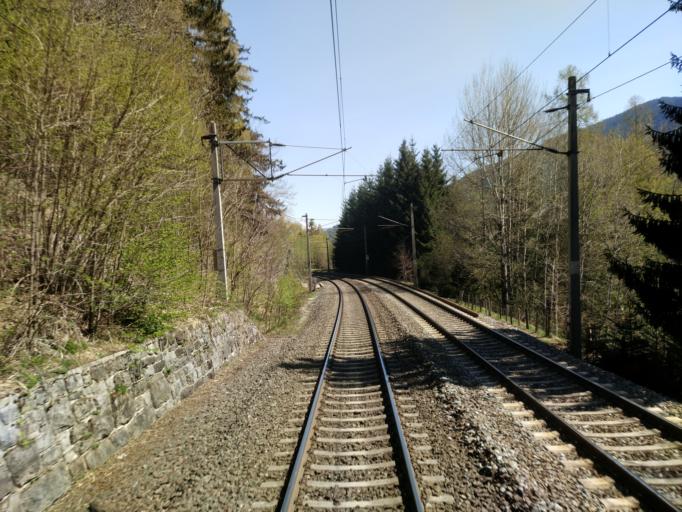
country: AT
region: Salzburg
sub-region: Politischer Bezirk Zell am See
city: Leogang
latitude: 47.4417
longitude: 12.7566
